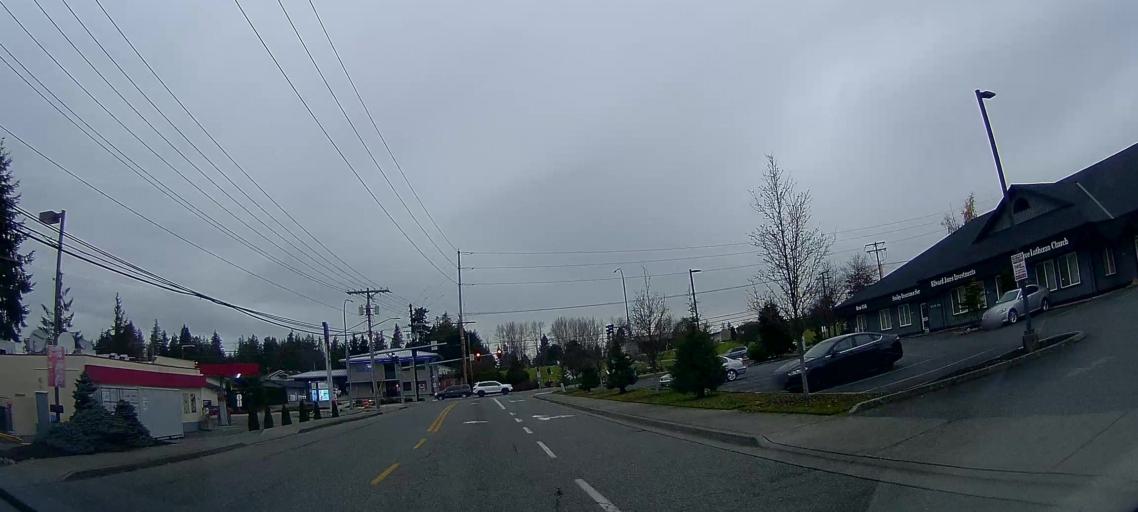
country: US
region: Washington
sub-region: Skagit County
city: Mount Vernon
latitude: 48.4350
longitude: -122.3189
